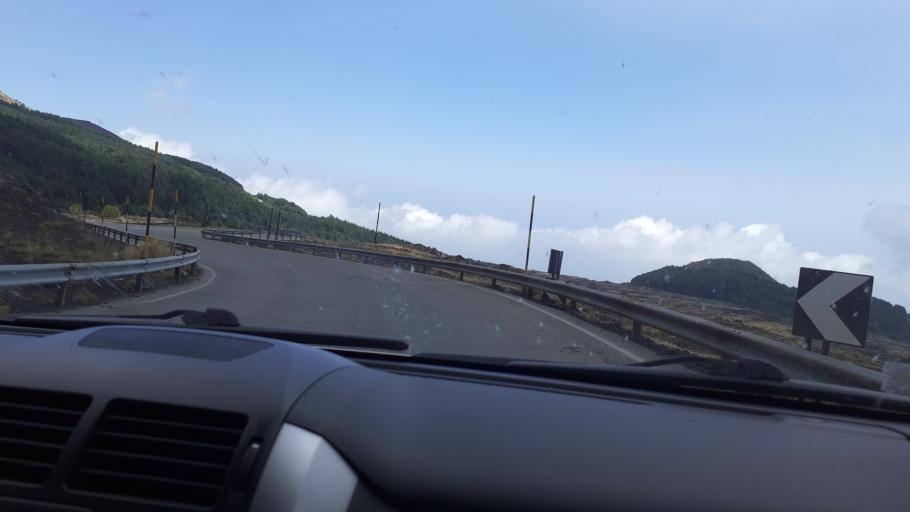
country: IT
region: Sicily
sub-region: Catania
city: Nicolosi
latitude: 37.6970
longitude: 15.0114
